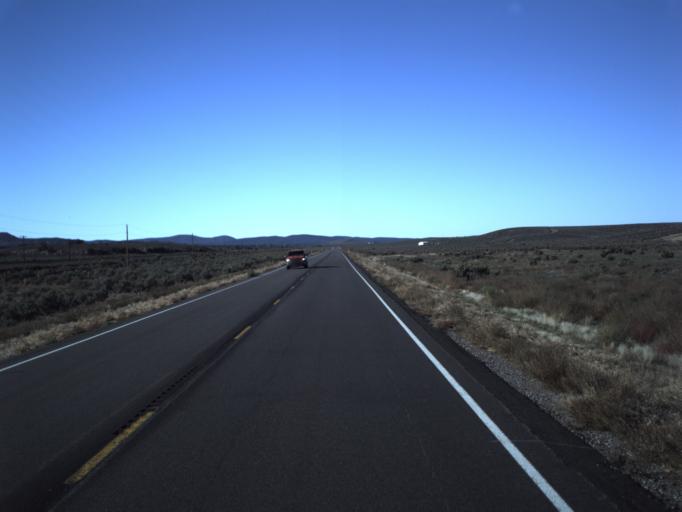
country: US
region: Utah
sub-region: Washington County
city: Enterprise
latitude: 37.7738
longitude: -113.9739
